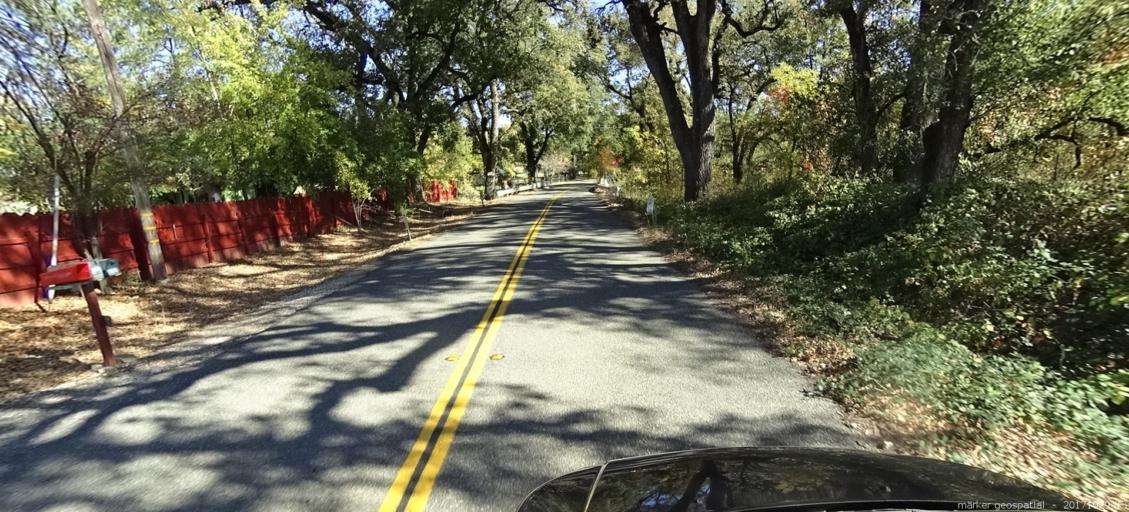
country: US
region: California
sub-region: Shasta County
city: Shasta
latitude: 40.4801
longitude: -122.5885
